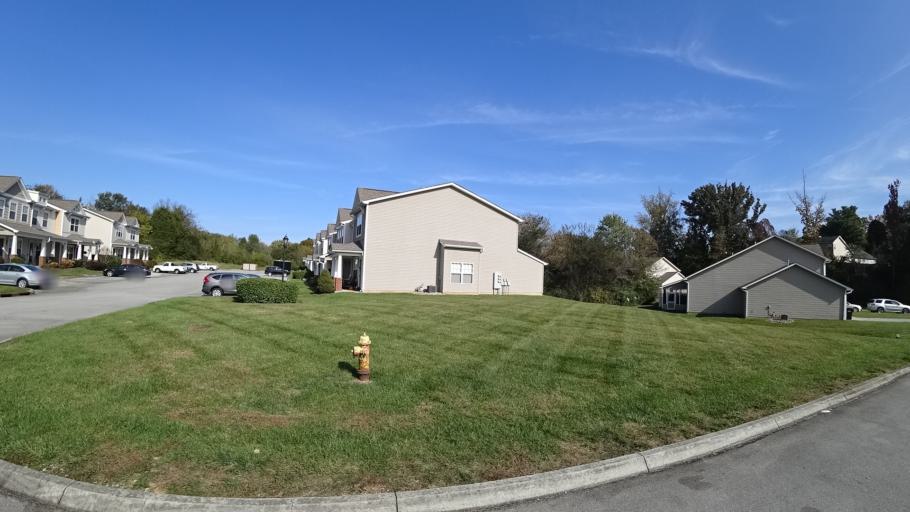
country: US
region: Tennessee
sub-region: Knox County
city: Farragut
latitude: 35.9301
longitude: -84.1528
